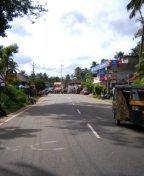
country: IN
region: Kerala
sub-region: Thrissur District
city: Trichur
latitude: 10.5242
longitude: 76.3525
